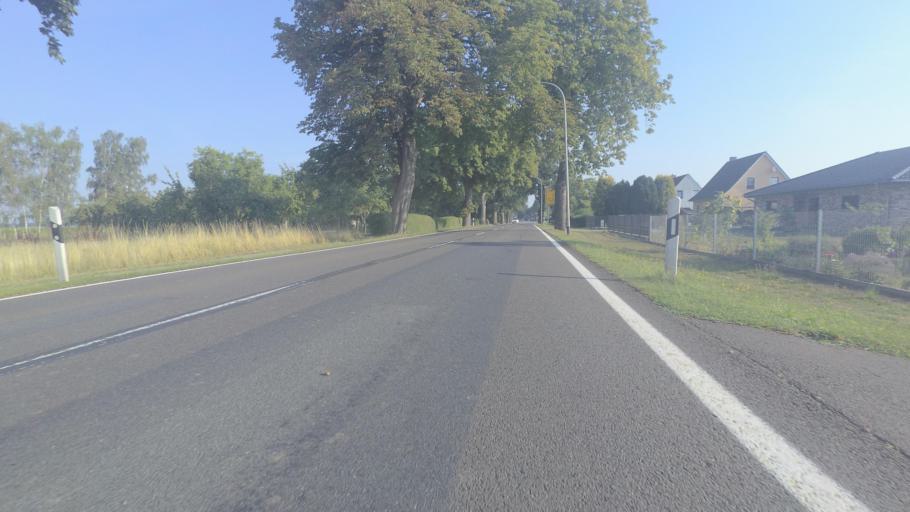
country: DE
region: Mecklenburg-Vorpommern
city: Grimmen
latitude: 54.0521
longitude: 13.1183
